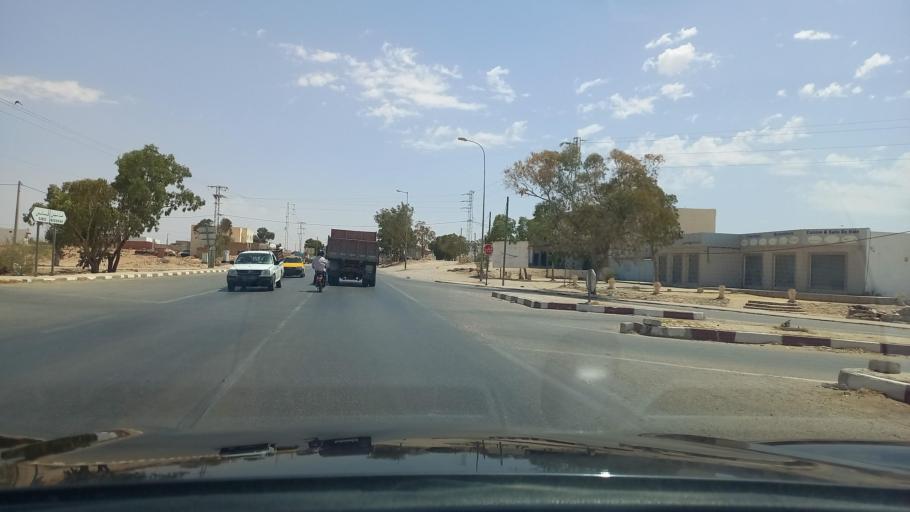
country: TN
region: Madanin
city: Medenine
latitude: 33.3726
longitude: 10.4471
